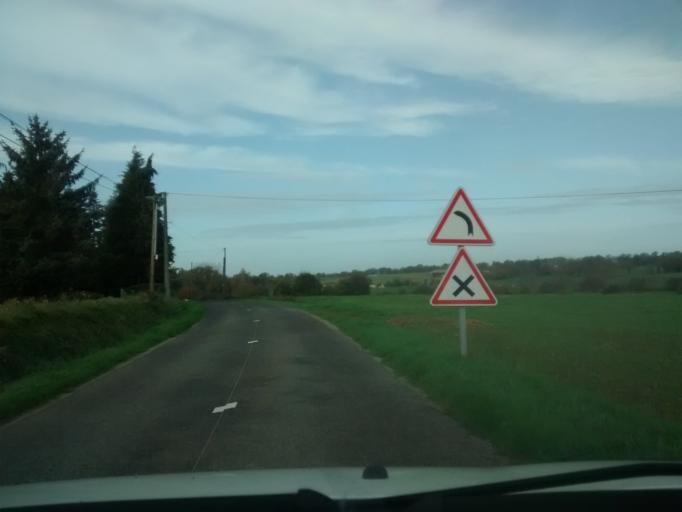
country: FR
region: Brittany
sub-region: Departement d'Ille-et-Vilaine
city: Brece
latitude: 48.1173
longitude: -1.4958
